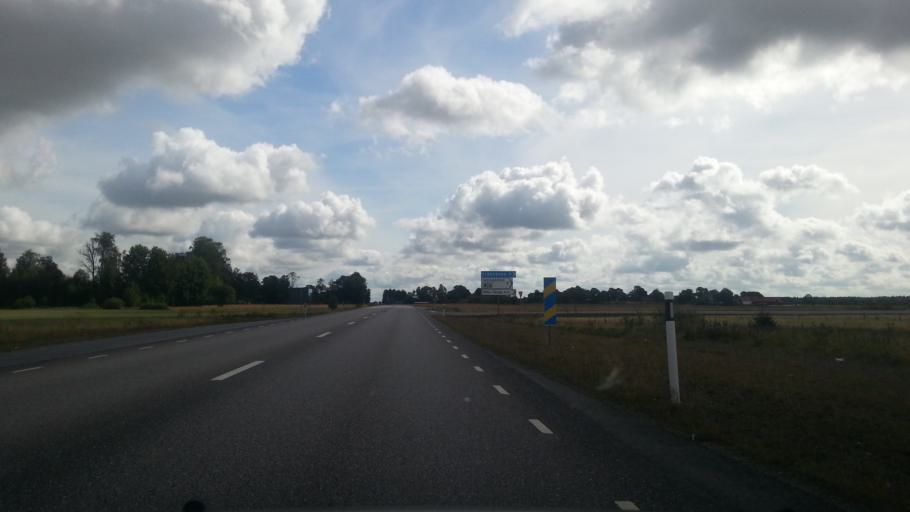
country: SE
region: Vaestra Goetaland
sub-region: Grastorps Kommun
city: Graestorp
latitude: 58.3972
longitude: 12.7957
